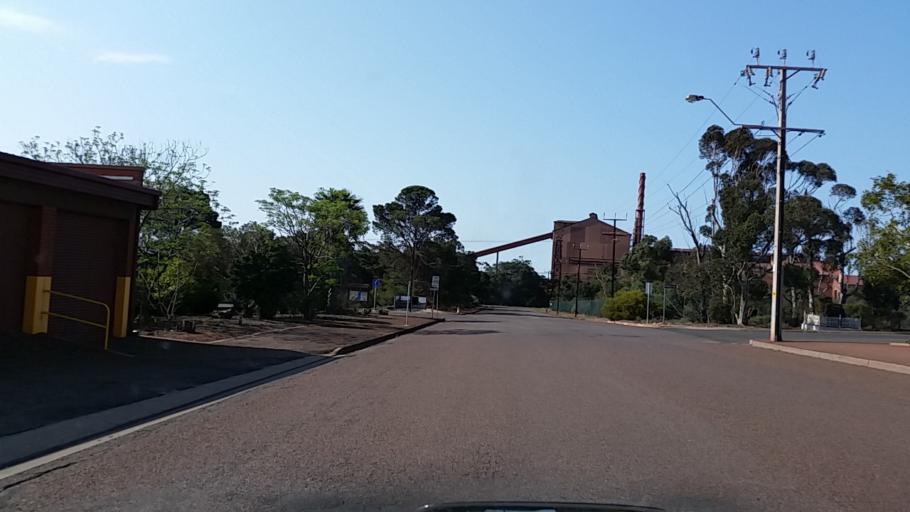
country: AU
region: South Australia
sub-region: Whyalla
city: Whyalla
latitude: -33.0353
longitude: 137.5877
